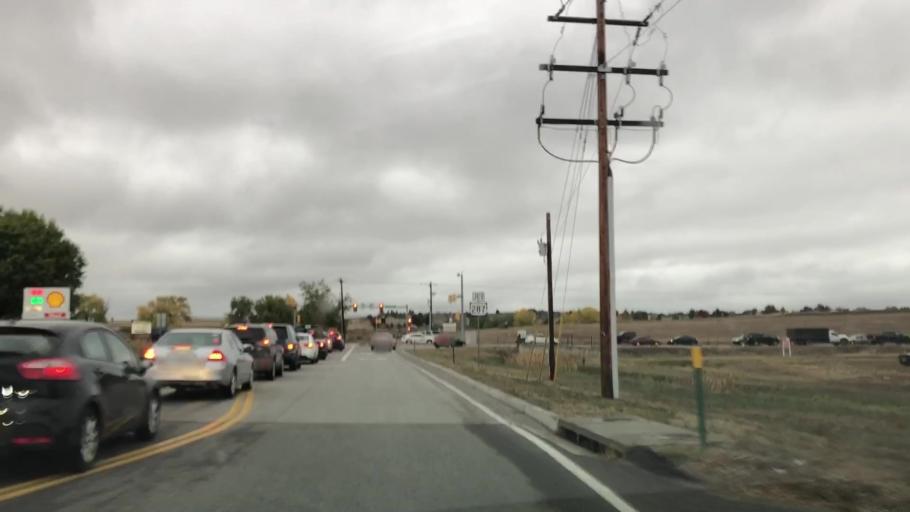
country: US
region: Colorado
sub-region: Larimer County
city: Loveland
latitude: 40.4802
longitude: -105.0761
